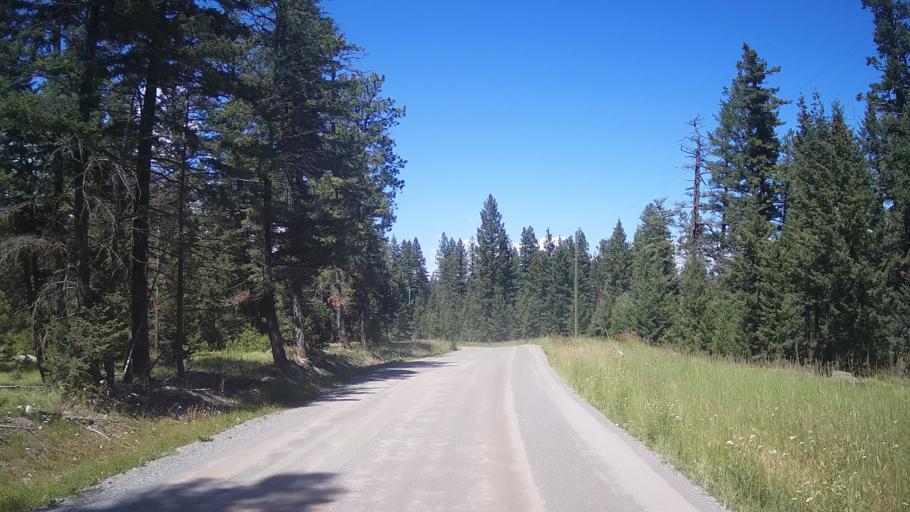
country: CA
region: British Columbia
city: Cache Creek
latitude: 51.2137
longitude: -121.6034
